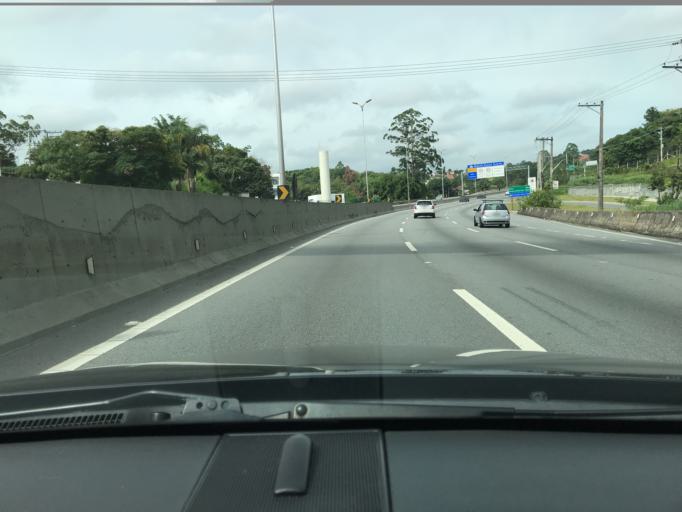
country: BR
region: Sao Paulo
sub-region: Taboao Da Serra
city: Taboao da Serra
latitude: -23.5907
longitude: -46.8180
